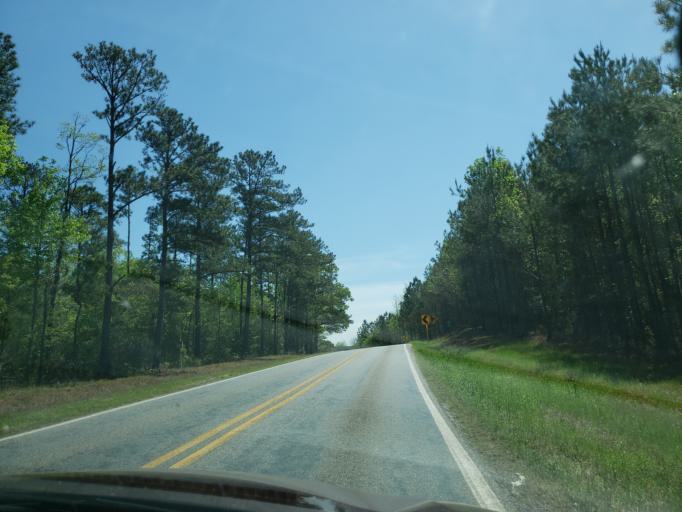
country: US
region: Alabama
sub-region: Tallapoosa County
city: Dadeville
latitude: 32.7060
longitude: -85.8189
